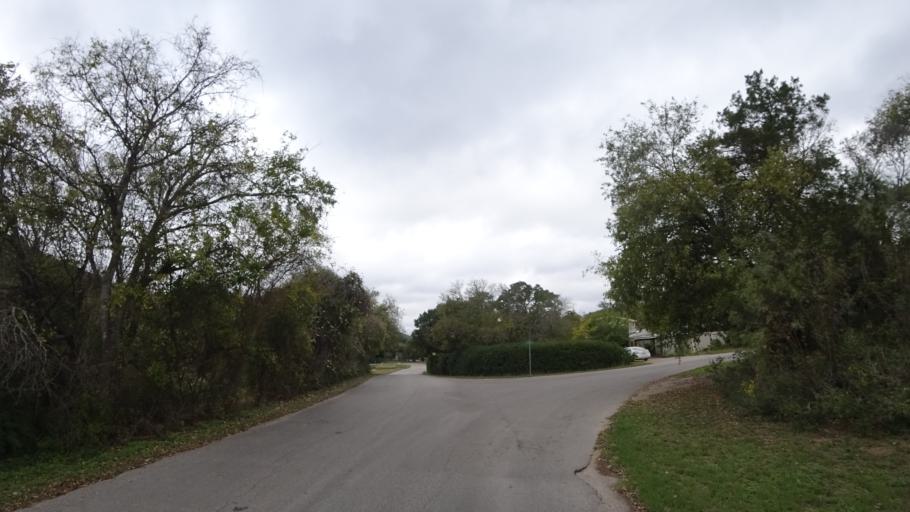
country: US
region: Texas
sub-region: Travis County
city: Bee Cave
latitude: 30.3301
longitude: -97.9284
